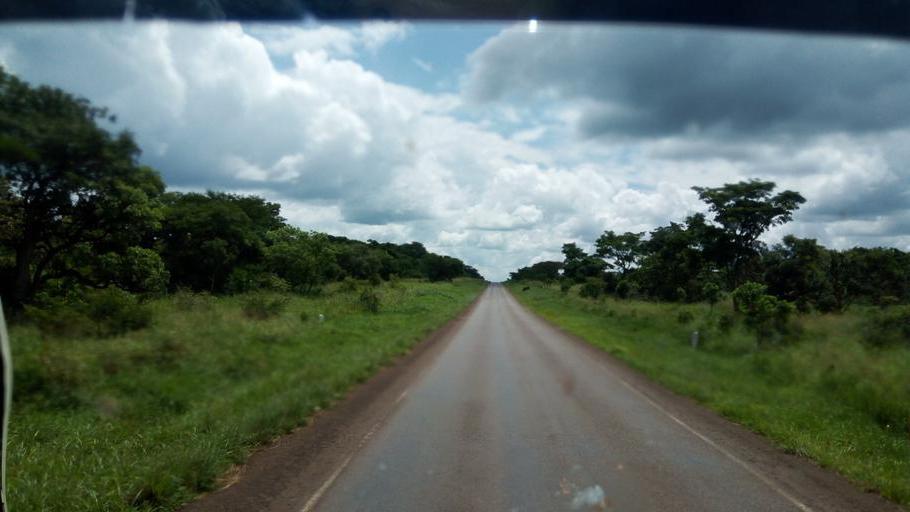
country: UG
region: Northern Region
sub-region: Oyam District
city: Oyam
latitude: 2.2836
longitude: 32.2173
